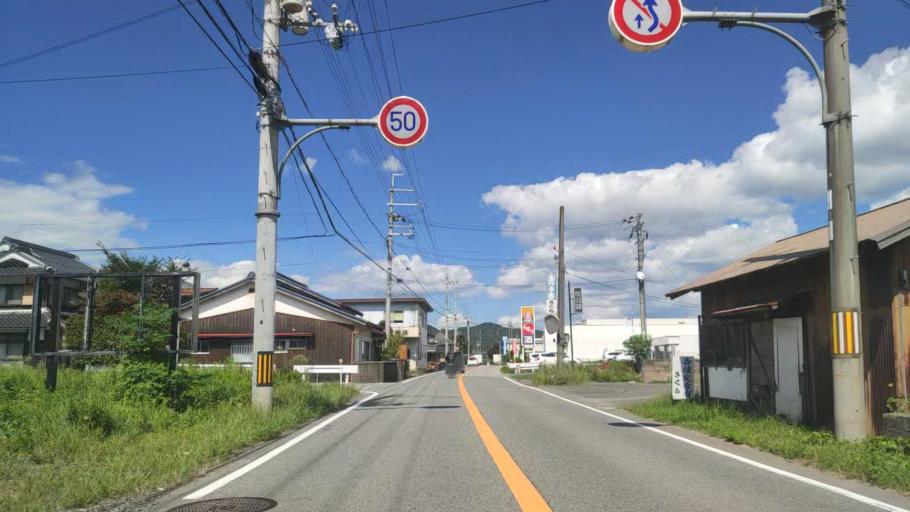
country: JP
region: Kyoto
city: Fukuchiyama
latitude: 35.2219
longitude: 135.1302
